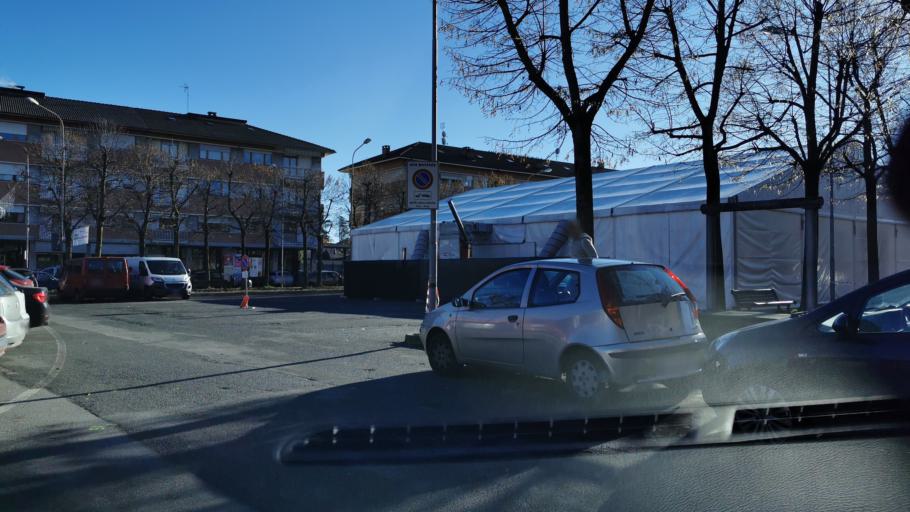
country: IT
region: Piedmont
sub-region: Provincia di Cuneo
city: Carru
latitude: 44.4792
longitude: 7.8743
